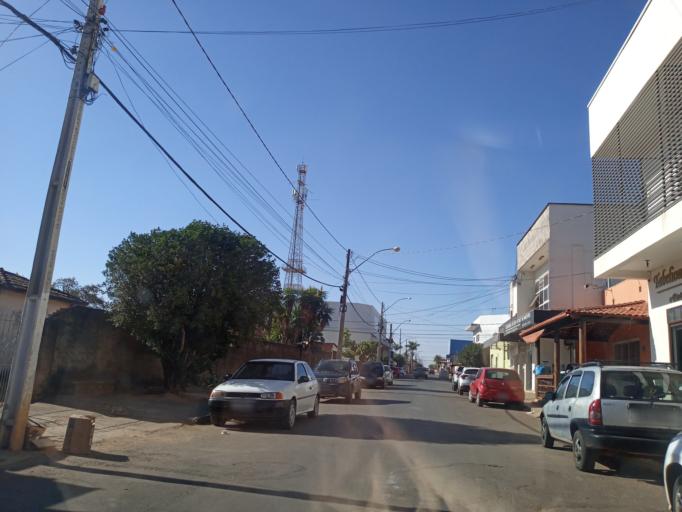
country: BR
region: Goias
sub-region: Abadiania
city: Abadiania
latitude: -16.0881
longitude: -48.5065
